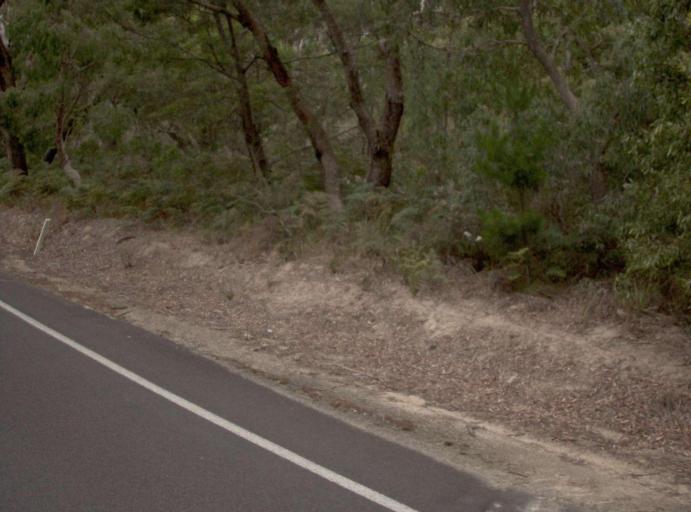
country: AU
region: Victoria
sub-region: Wellington
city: Sale
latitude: -38.2146
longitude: 147.0622
